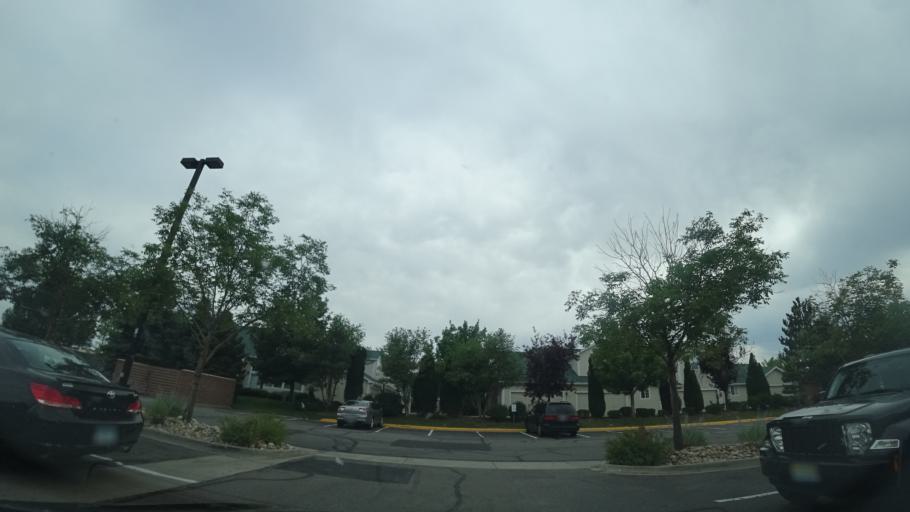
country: US
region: Colorado
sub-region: Jefferson County
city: Lakewood
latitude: 39.7064
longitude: -105.0824
